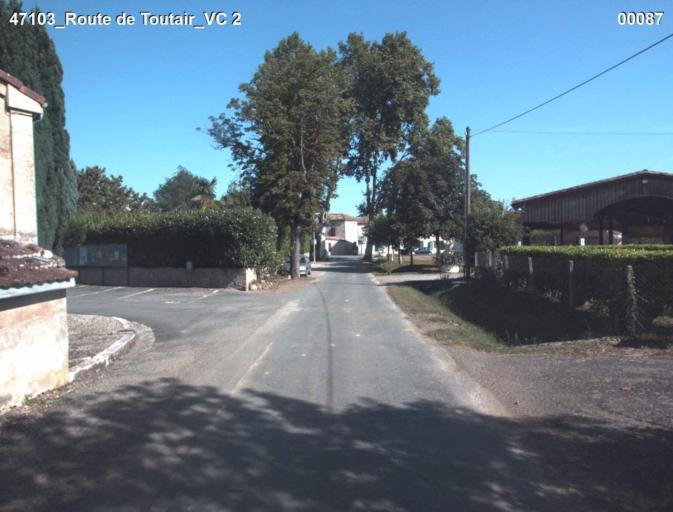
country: FR
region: Aquitaine
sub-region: Departement du Lot-et-Garonne
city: Nerac
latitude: 44.0845
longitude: 0.3218
